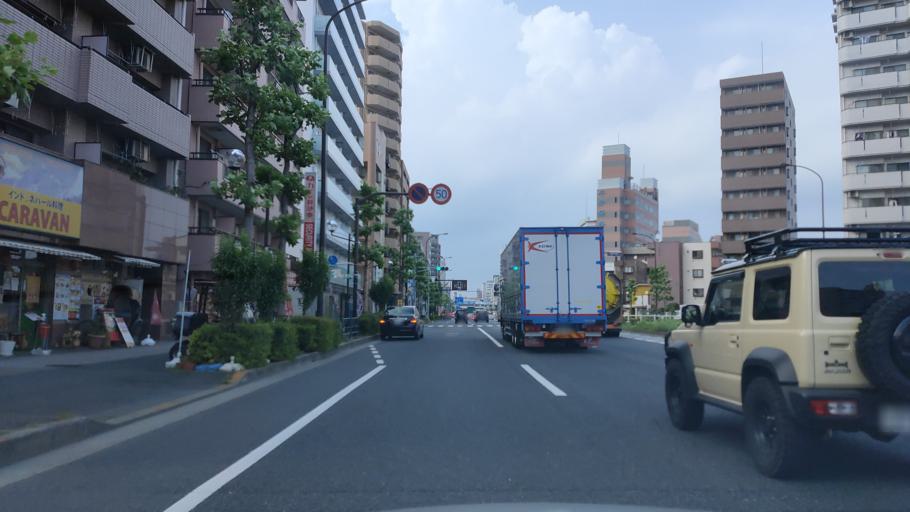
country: JP
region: Tokyo
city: Urayasu
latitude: 35.6567
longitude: 139.8725
